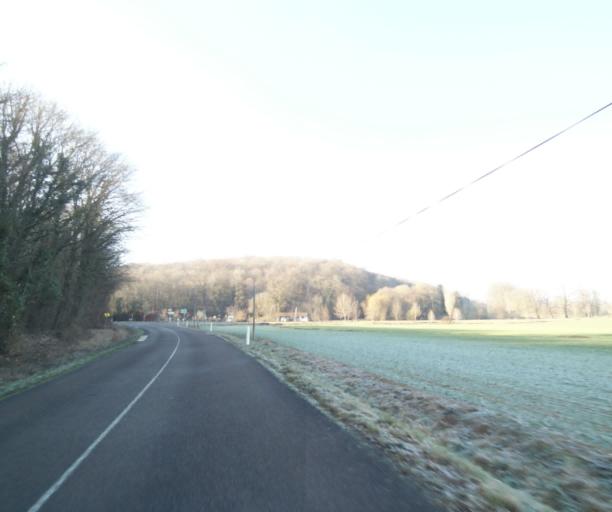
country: FR
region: Champagne-Ardenne
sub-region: Departement de la Haute-Marne
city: Bienville
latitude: 48.5547
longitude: 5.0888
